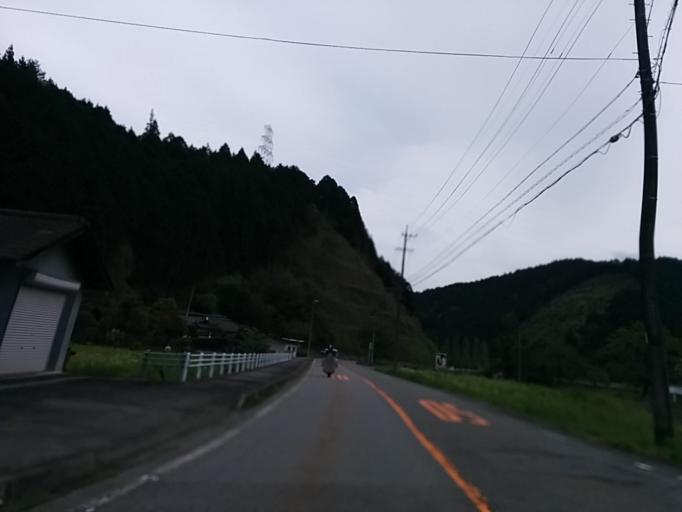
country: JP
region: Gifu
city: Gujo
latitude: 35.7398
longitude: 137.0533
